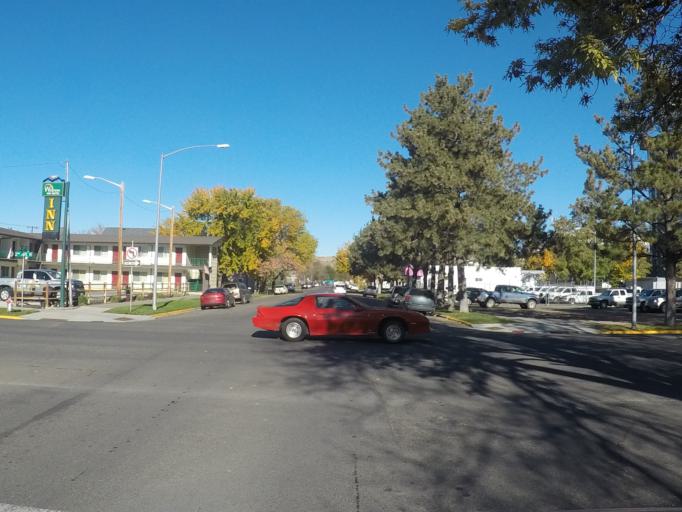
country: US
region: Montana
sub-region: Yellowstone County
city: Billings
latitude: 45.7799
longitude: -108.5126
